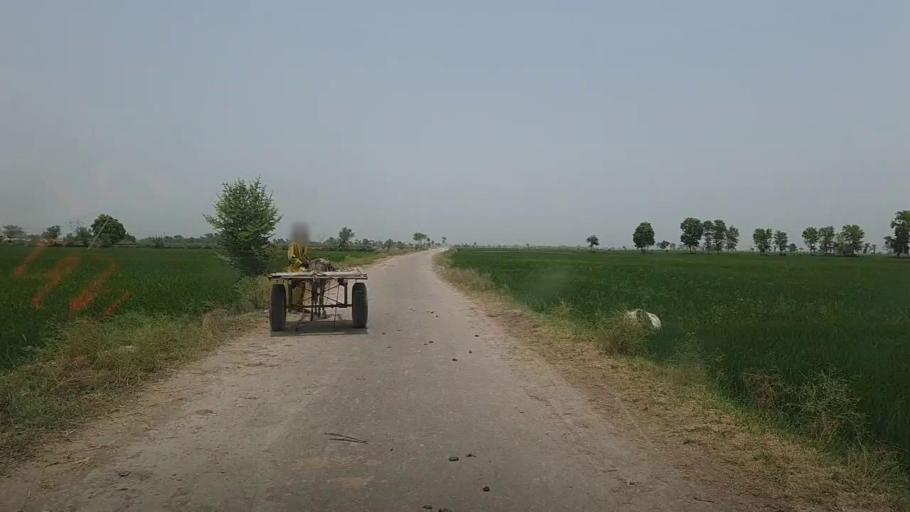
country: PK
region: Sindh
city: Sita Road
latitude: 27.0547
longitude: 67.8482
